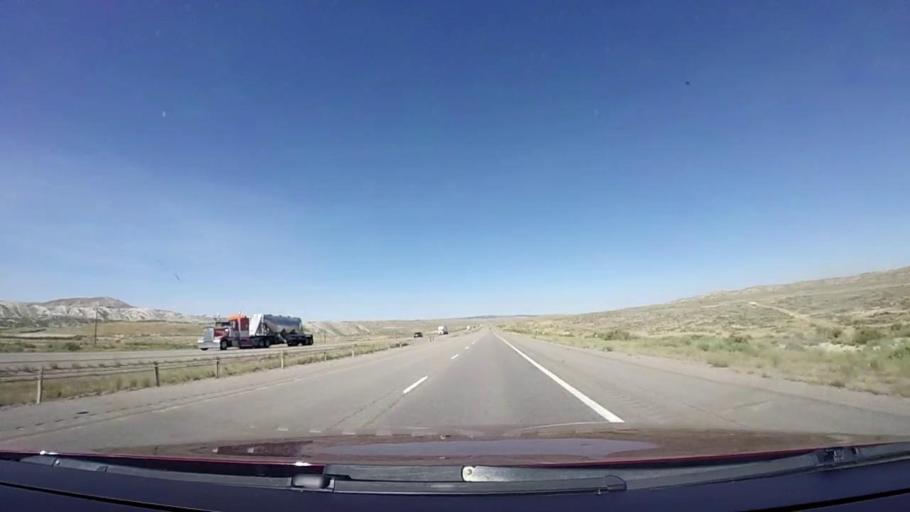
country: US
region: Wyoming
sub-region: Sweetwater County
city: Rock Springs
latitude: 41.6471
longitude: -108.6622
